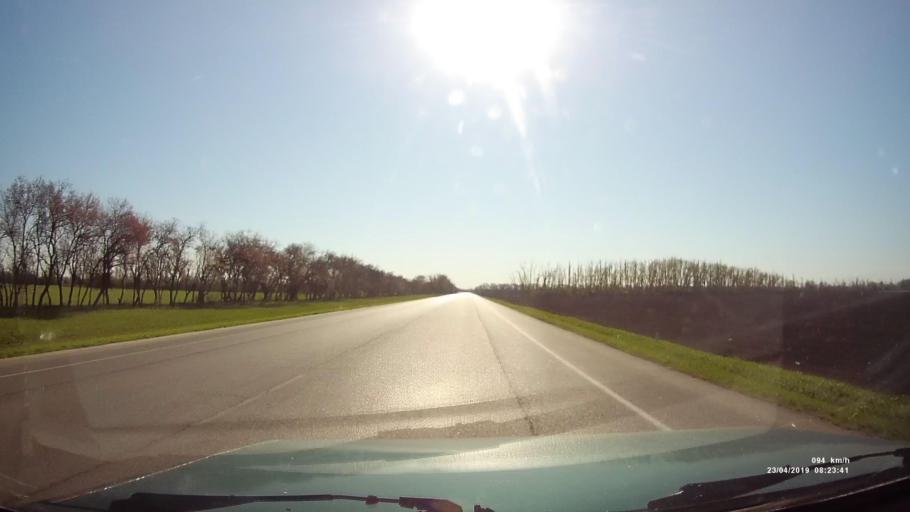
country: RU
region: Rostov
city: Tselina
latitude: 46.5313
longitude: 40.9334
